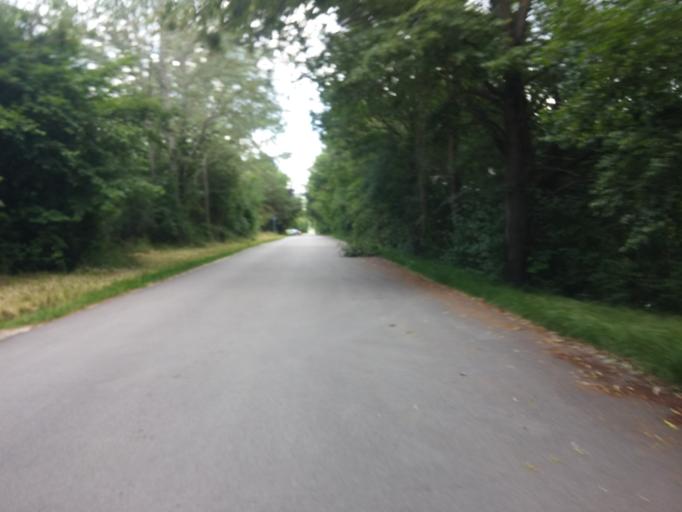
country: DE
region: Bavaria
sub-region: Upper Bavaria
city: Aschheim
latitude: 48.1789
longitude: 11.7019
